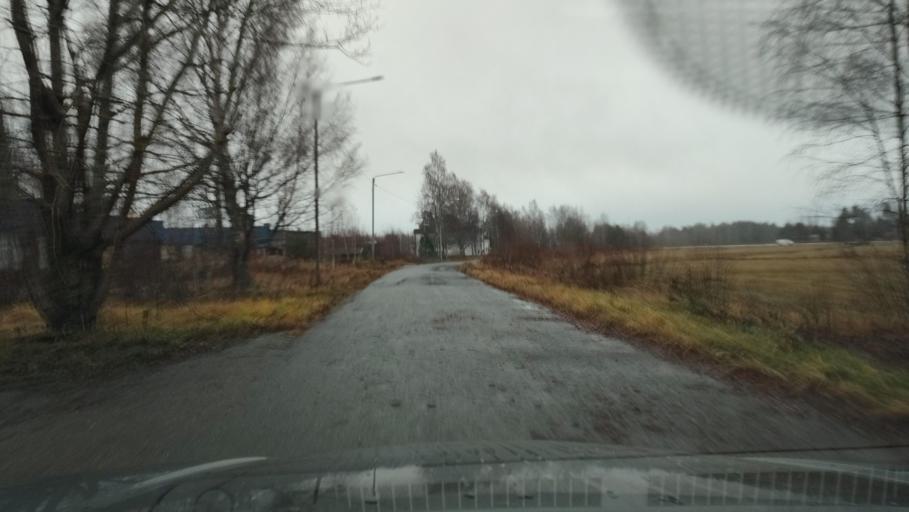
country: FI
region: Ostrobothnia
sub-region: Sydosterbotten
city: Kristinestad
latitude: 62.2637
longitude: 21.4791
